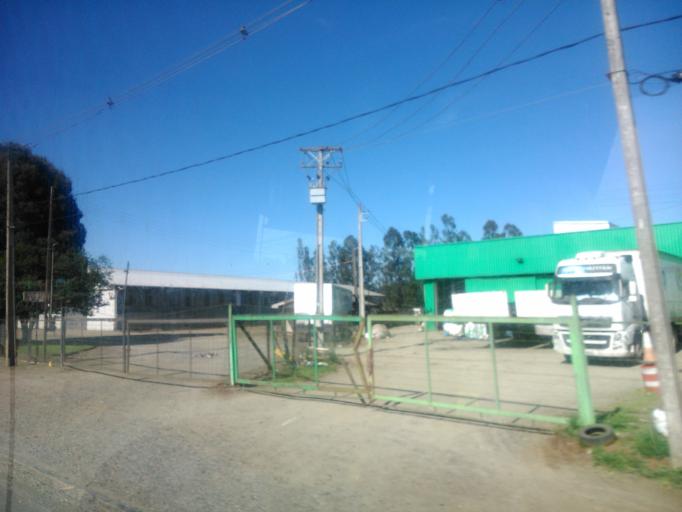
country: CL
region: Araucania
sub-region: Provincia de Cautin
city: Temuco
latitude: -38.7777
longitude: -72.6085
